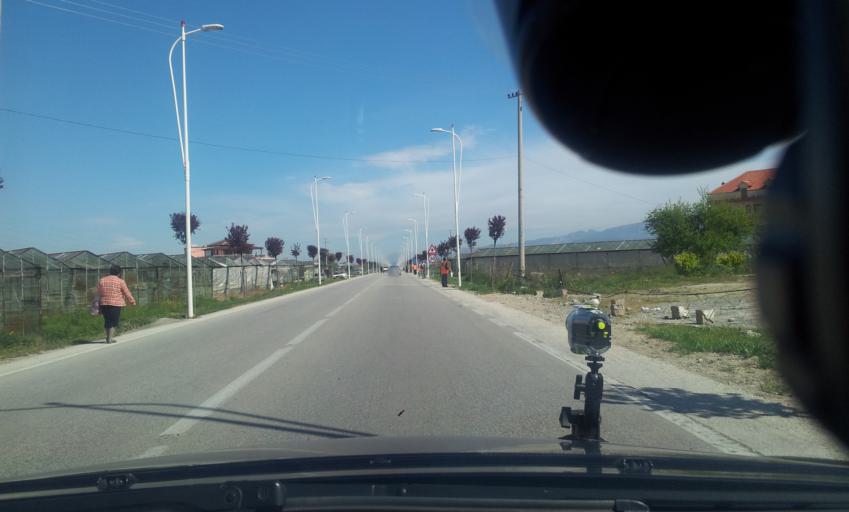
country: AL
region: Tirane
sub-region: Rrethi i Tiranes
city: Berxull
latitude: 41.3768
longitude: 19.7039
